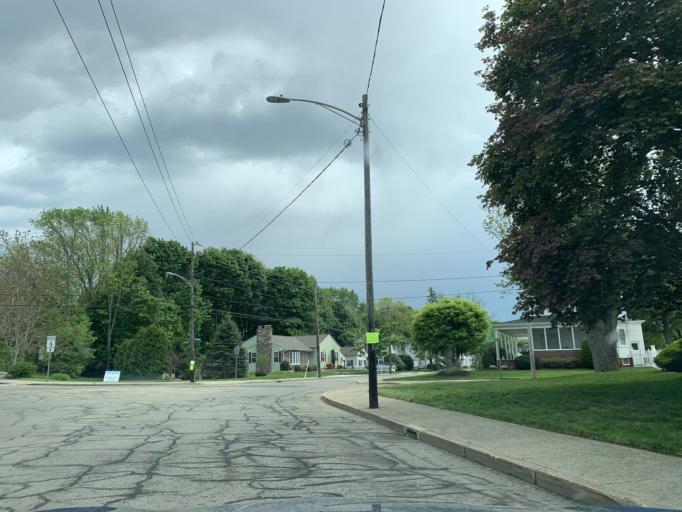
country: US
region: Rhode Island
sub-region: Providence County
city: Cranston
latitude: 41.7770
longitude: -71.4691
